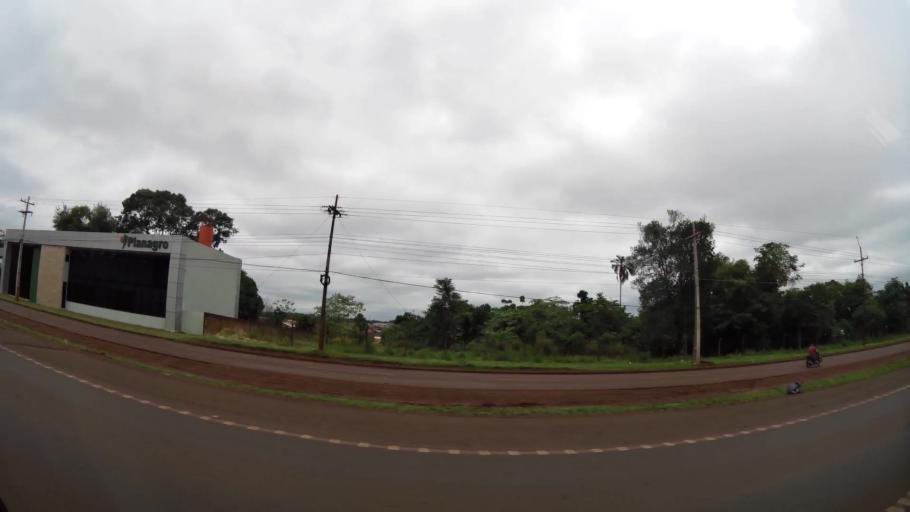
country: PY
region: Alto Parana
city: Ciudad del Este
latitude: -25.4953
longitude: -54.6954
